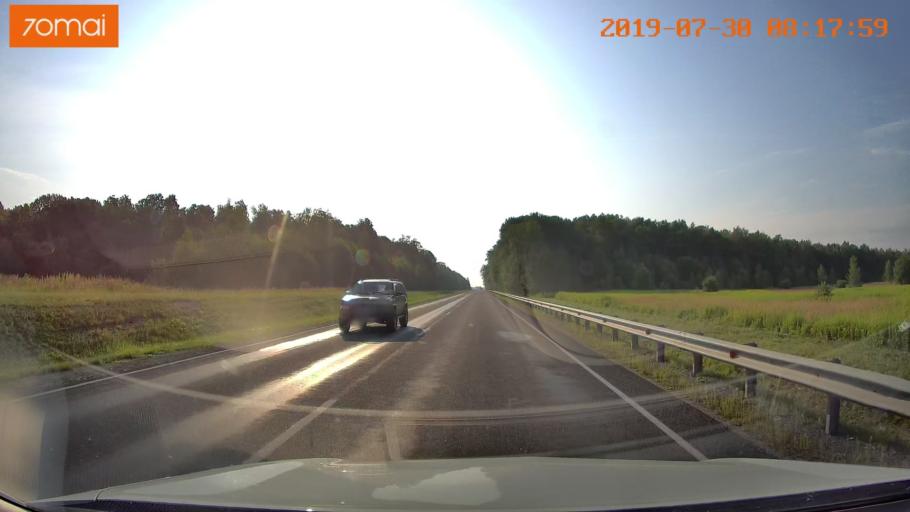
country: RU
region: Kaliningrad
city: Zheleznodorozhnyy
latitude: 54.6342
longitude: 21.4518
